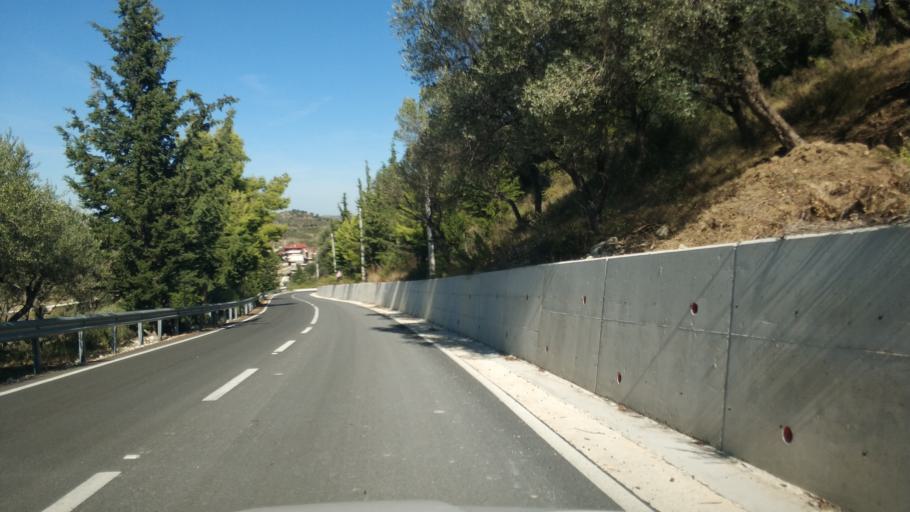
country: AL
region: Vlore
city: Vlore
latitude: 40.4521
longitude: 19.5152
